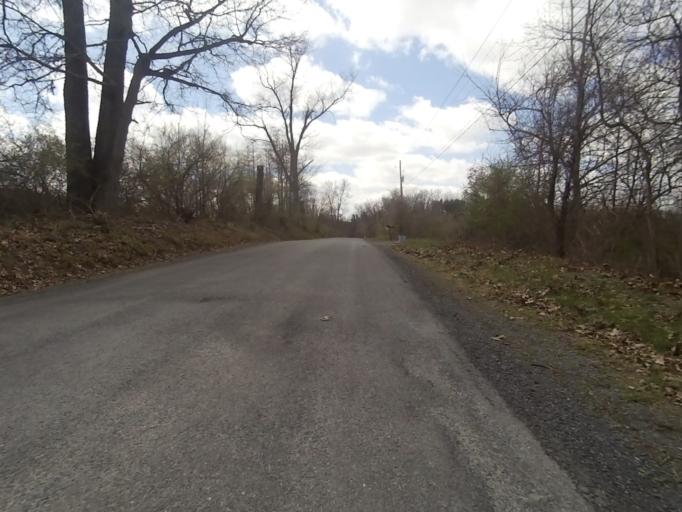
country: US
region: Pennsylvania
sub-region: Centre County
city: Bellefonte
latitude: 40.8756
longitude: -77.8106
